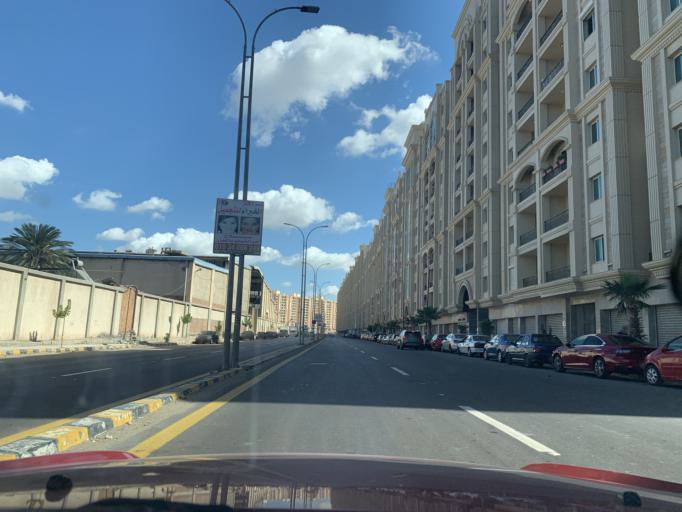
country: EG
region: Alexandria
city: Alexandria
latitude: 31.2185
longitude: 29.9503
